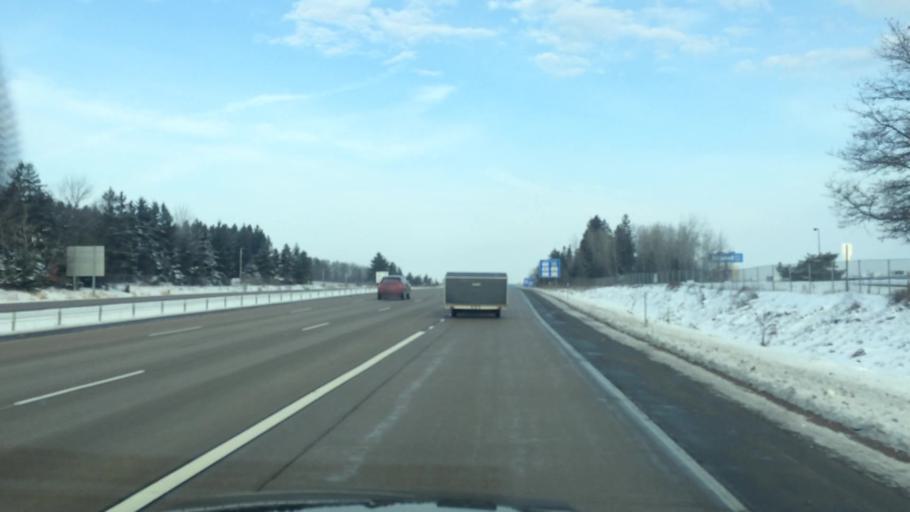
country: US
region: Wisconsin
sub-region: Marathon County
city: Rib Mountain
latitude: 44.9159
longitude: -89.6536
